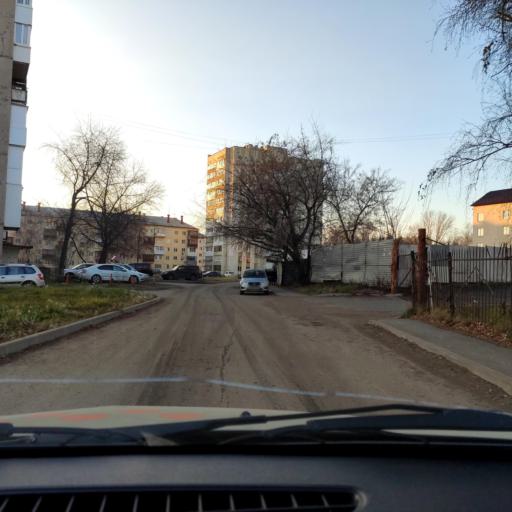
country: RU
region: Bashkortostan
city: Ufa
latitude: 54.8029
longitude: 56.1228
